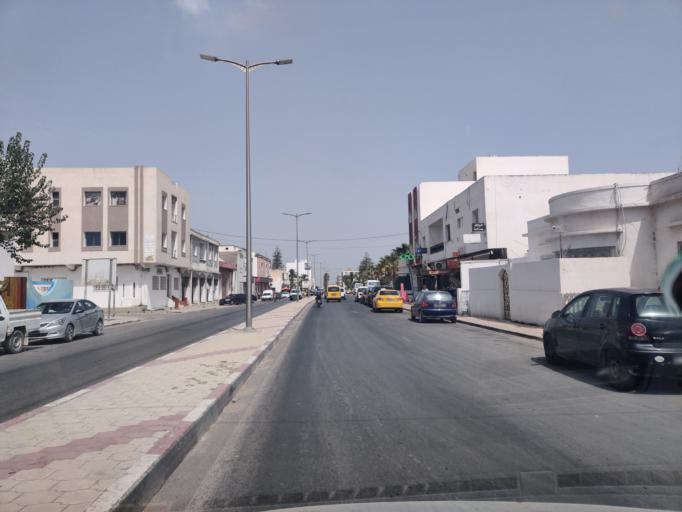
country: TN
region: Nabul
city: Bu `Urqub
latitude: 36.5955
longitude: 10.5011
